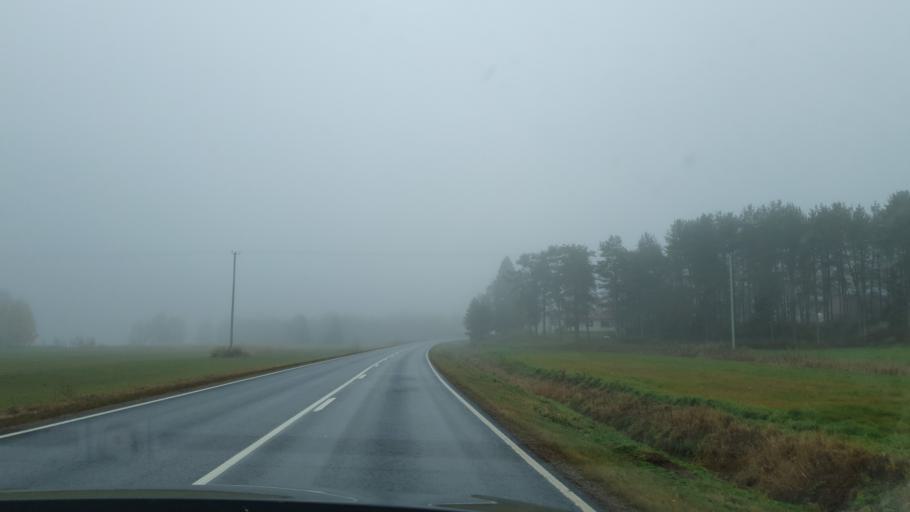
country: FI
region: Lapland
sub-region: Rovaniemi
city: Rovaniemi
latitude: 66.8076
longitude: 25.4105
